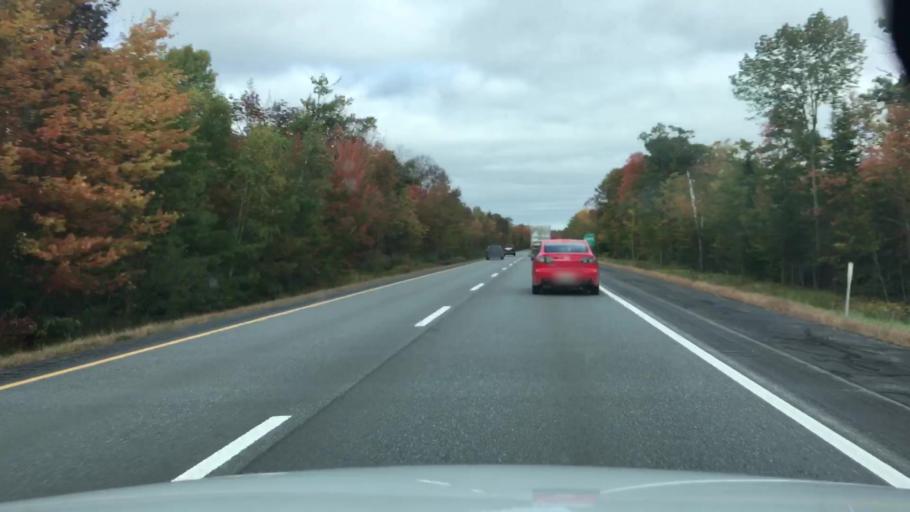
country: US
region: Maine
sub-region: Somerset County
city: Palmyra
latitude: 44.8288
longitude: -69.3194
